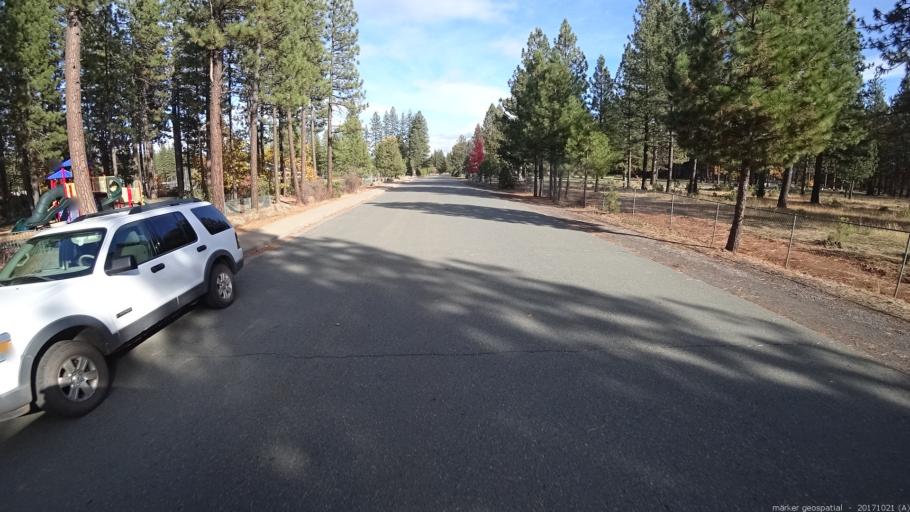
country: US
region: California
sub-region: Shasta County
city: Burney
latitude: 40.8811
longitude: -121.6540
